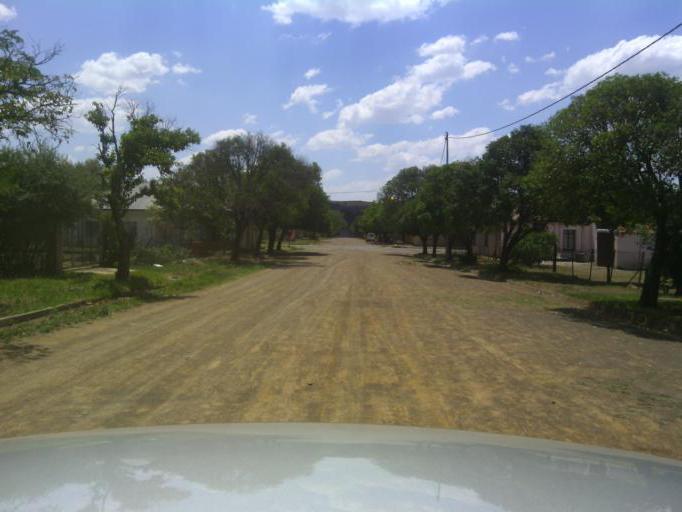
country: ZA
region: Orange Free State
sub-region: Xhariep District Municipality
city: Dewetsdorp
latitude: -29.5825
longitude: 26.6678
